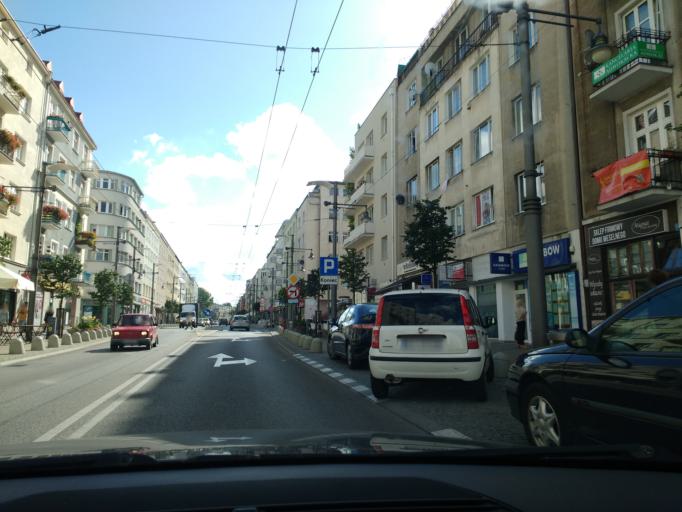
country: PL
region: Pomeranian Voivodeship
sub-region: Gdynia
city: Gdynia
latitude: 54.5121
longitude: 18.5393
